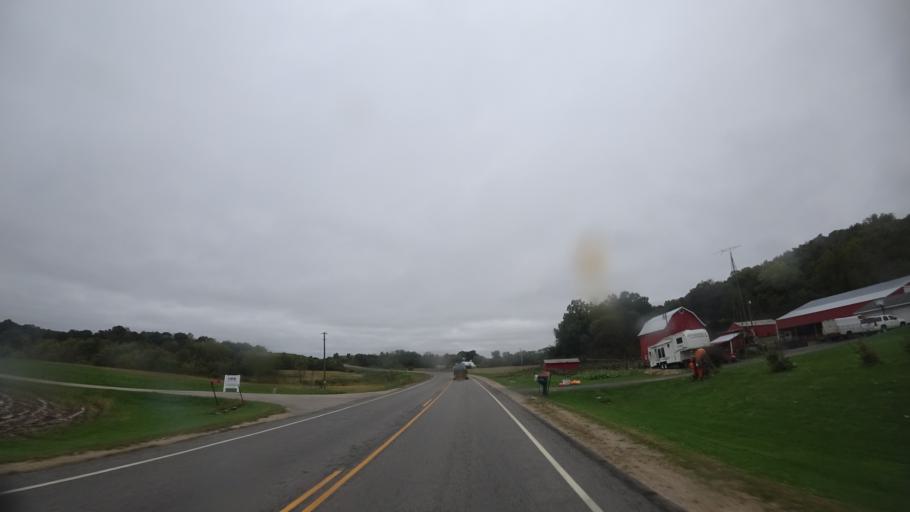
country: US
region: Wisconsin
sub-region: Crawford County
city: Prairie du Chien
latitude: 43.0255
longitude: -91.0256
